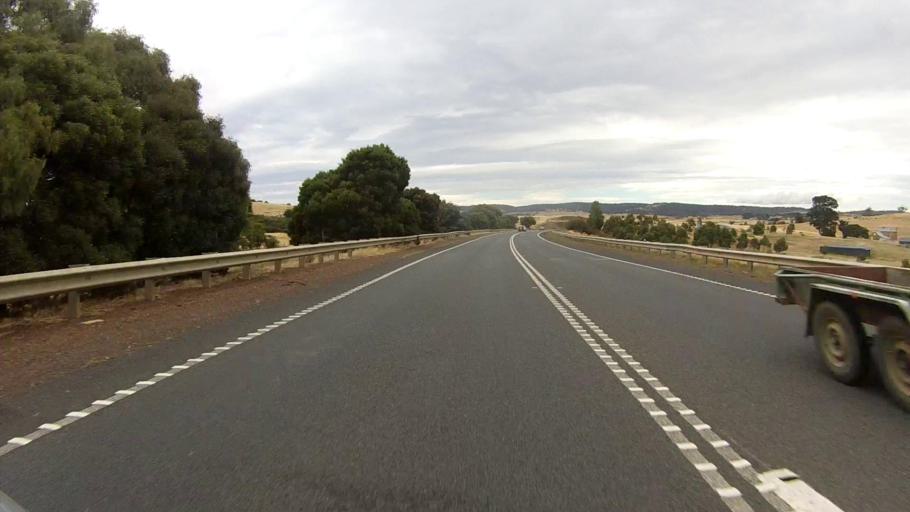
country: AU
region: Tasmania
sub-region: Brighton
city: Bridgewater
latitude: -42.3272
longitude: 147.3434
